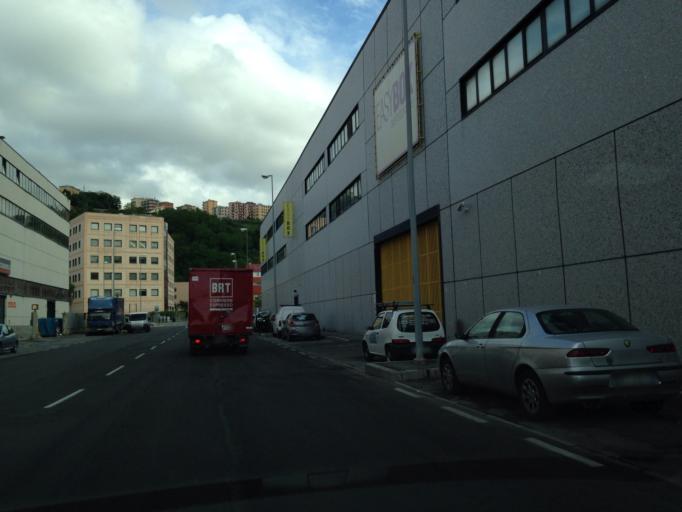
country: IT
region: Liguria
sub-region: Provincia di Genova
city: San Teodoro
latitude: 44.4198
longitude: 8.8818
